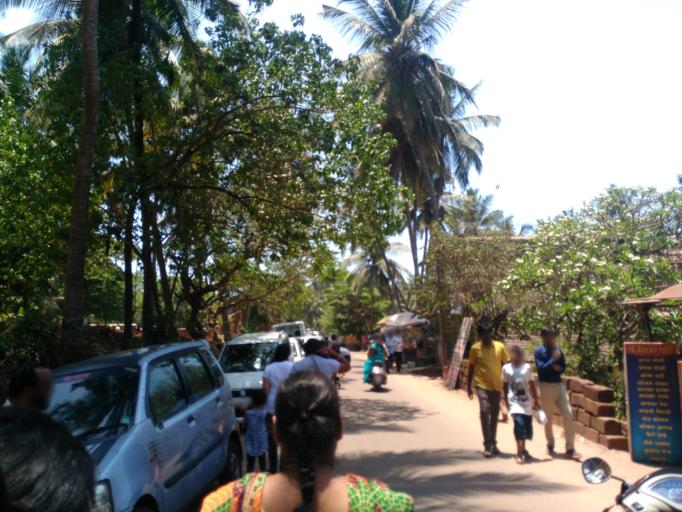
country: IN
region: Maharashtra
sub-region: Ratnagiri
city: Ratnagiri
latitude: 17.1474
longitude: 73.2678
